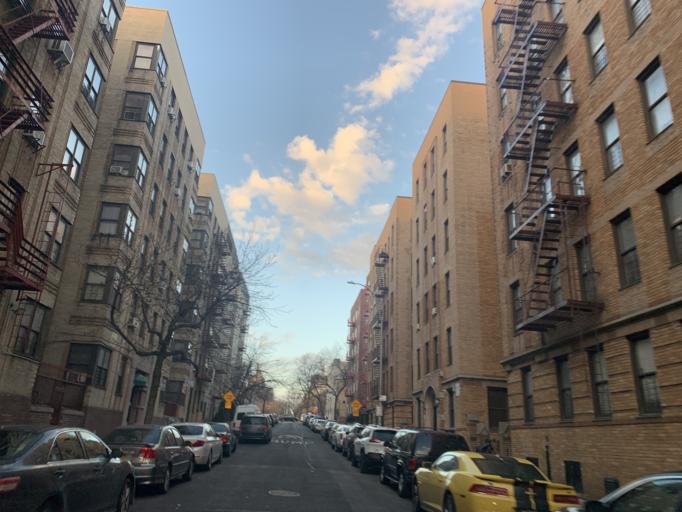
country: US
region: New York
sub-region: Bronx
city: The Bronx
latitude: 40.8554
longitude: -73.8687
